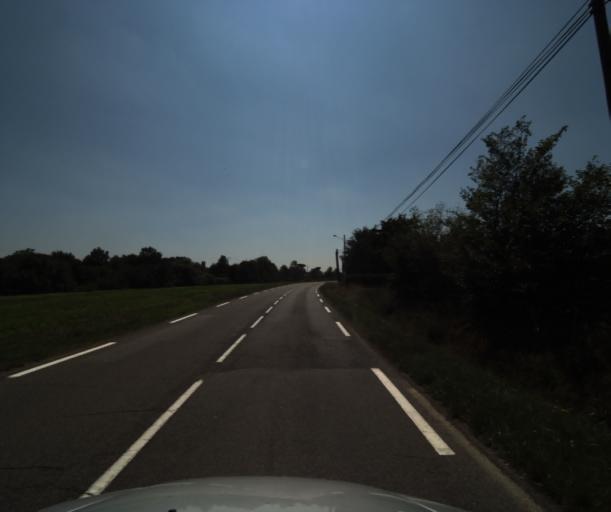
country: FR
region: Midi-Pyrenees
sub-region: Departement de la Haute-Garonne
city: Labastidette
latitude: 43.4562
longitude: 1.2894
